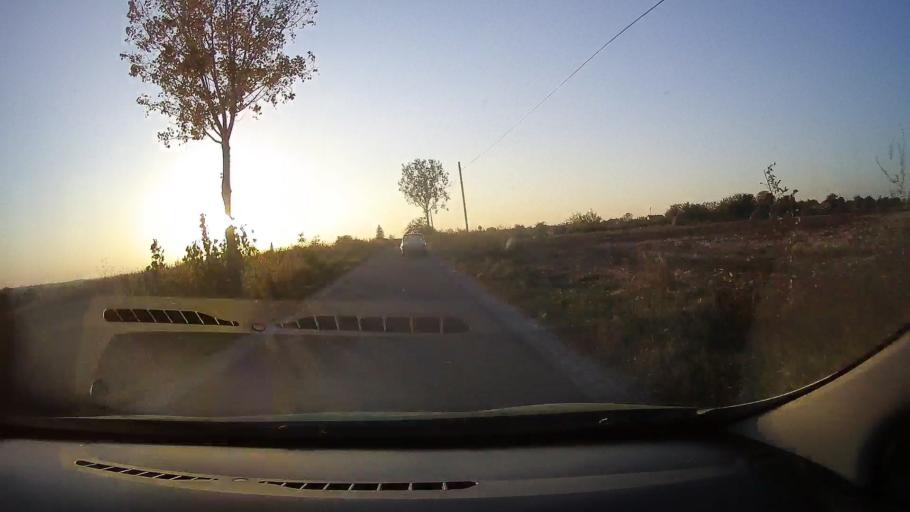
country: RO
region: Bihor
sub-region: Comuna Rosiori
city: Rosiori
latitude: 47.2567
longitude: 21.9669
